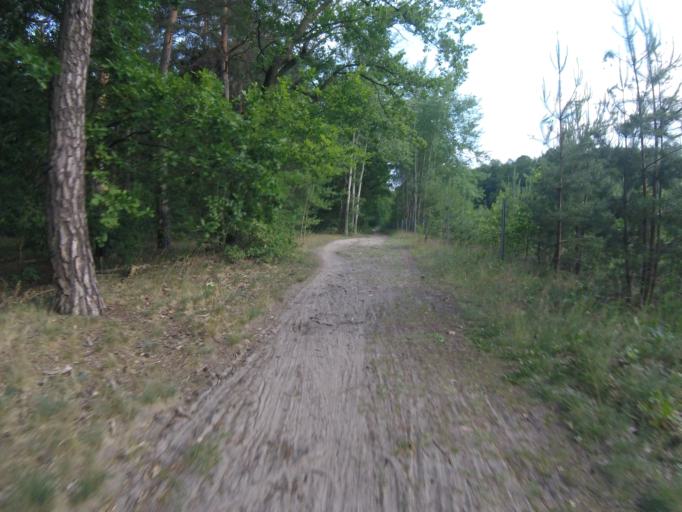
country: DE
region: Brandenburg
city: Konigs Wusterhausen
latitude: 52.2915
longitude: 13.6380
